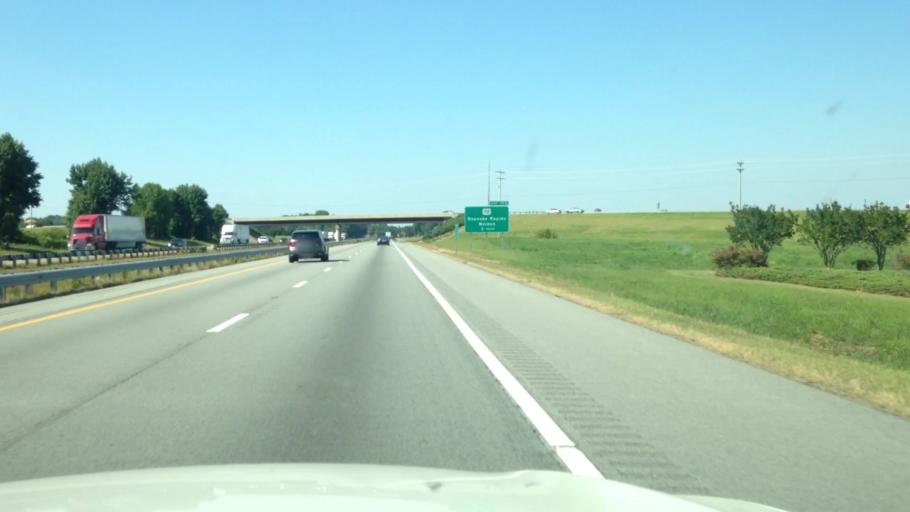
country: US
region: North Carolina
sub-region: Halifax County
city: Weldon
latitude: 36.3981
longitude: -77.6450
